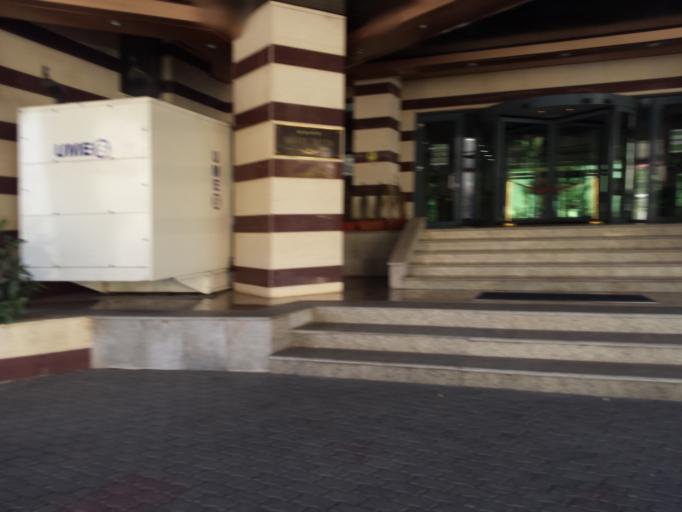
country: RO
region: Tulcea
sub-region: Municipiul Tulcea
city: Tulcea
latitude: 45.1803
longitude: 28.8044
